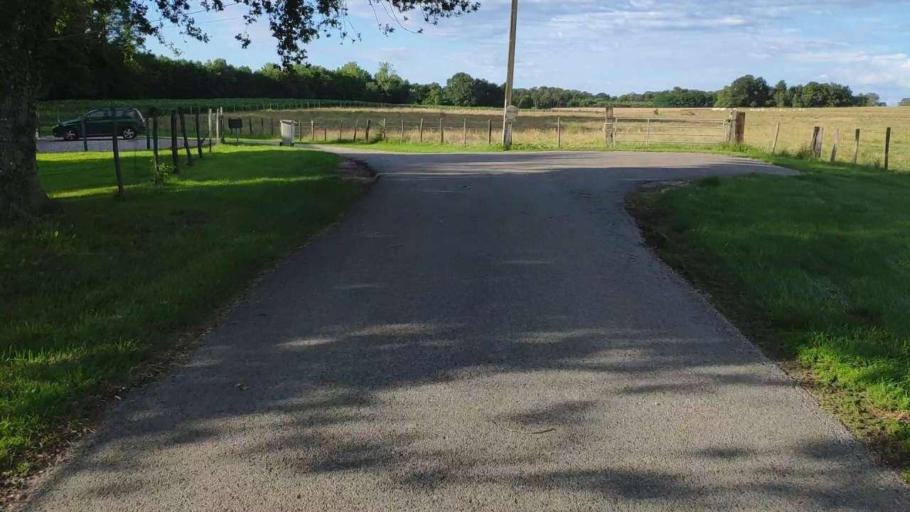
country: FR
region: Franche-Comte
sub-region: Departement du Jura
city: Bletterans
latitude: 46.7848
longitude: 5.4953
